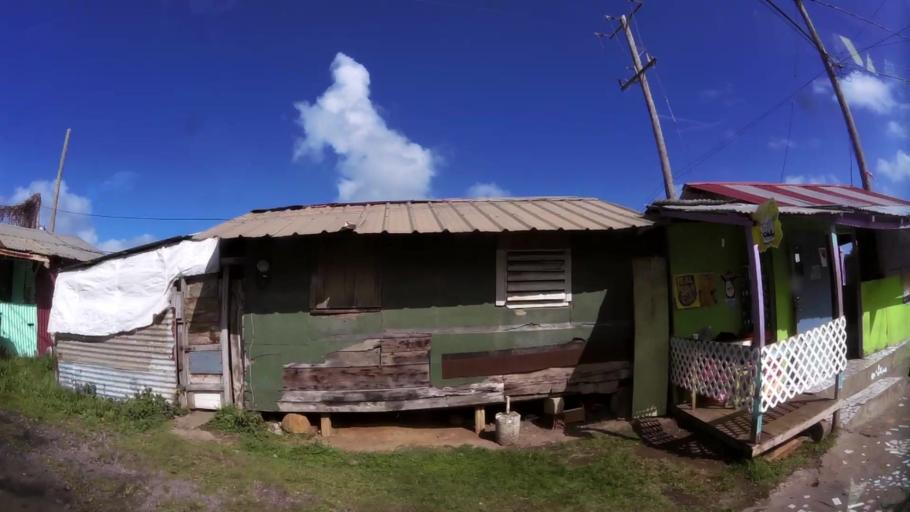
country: DM
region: Saint Andrew
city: Marigot
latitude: 15.5410
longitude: -61.2865
